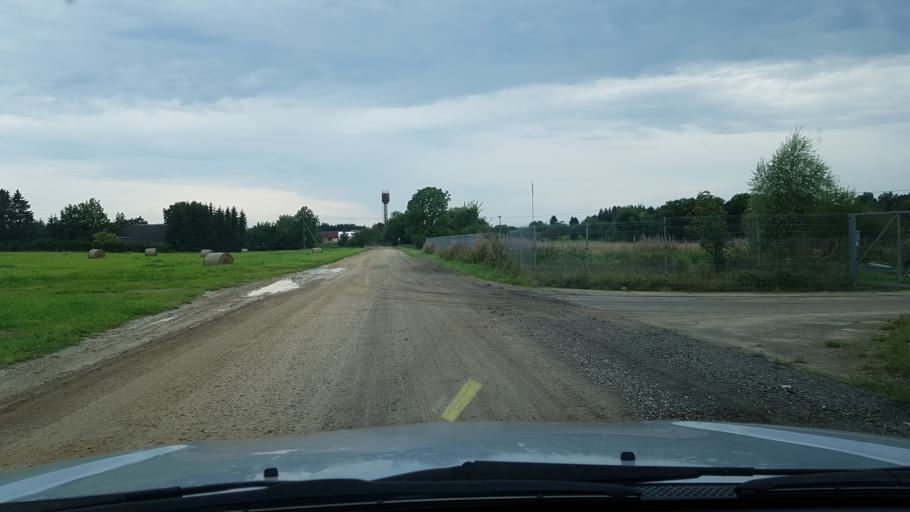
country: EE
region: Harju
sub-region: Rae vald
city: Vaida
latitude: 59.3176
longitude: 24.9390
